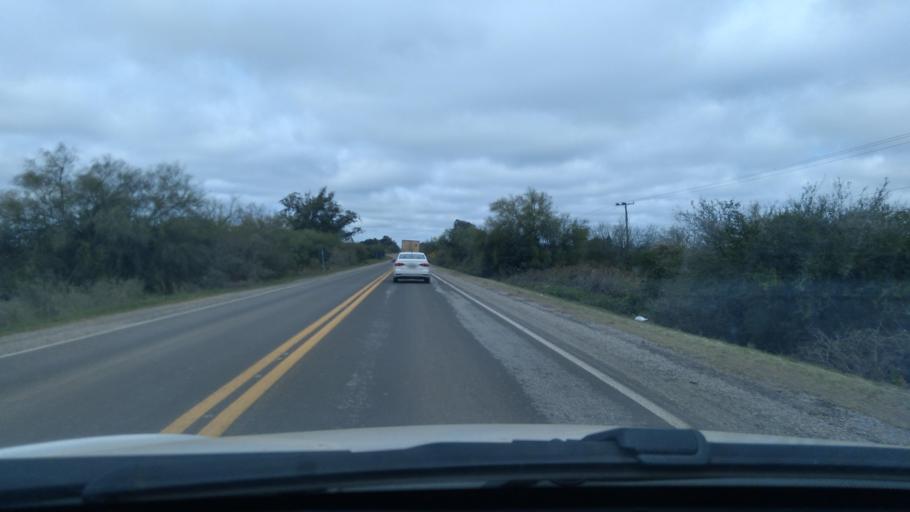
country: BR
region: Rio Grande do Sul
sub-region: Dom Pedrito
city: Dom Pedrito
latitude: -30.9808
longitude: -54.6420
